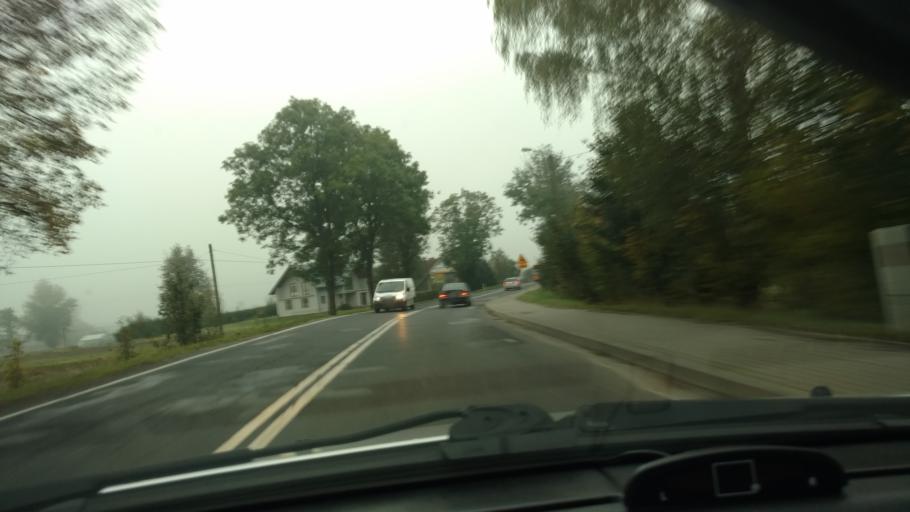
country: PL
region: Subcarpathian Voivodeship
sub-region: Powiat strzyzowski
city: Wisniowa
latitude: 49.8703
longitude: 21.6635
